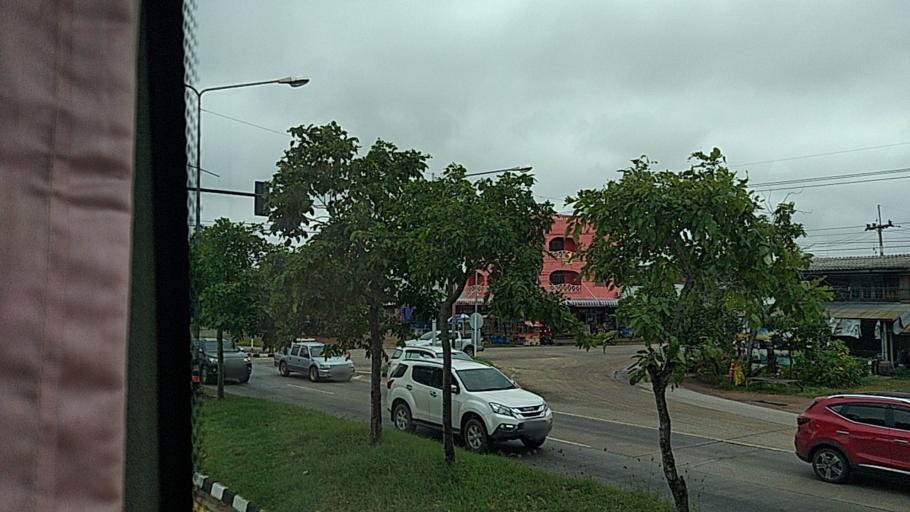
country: TH
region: Nakhon Ratchasima
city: Non Daeng
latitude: 15.4593
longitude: 102.5034
